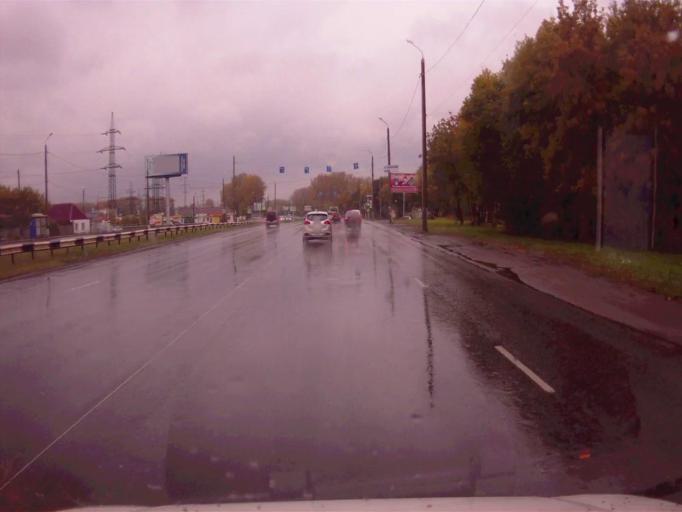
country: RU
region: Chelyabinsk
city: Dolgoderevenskoye
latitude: 55.2394
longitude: 61.3613
